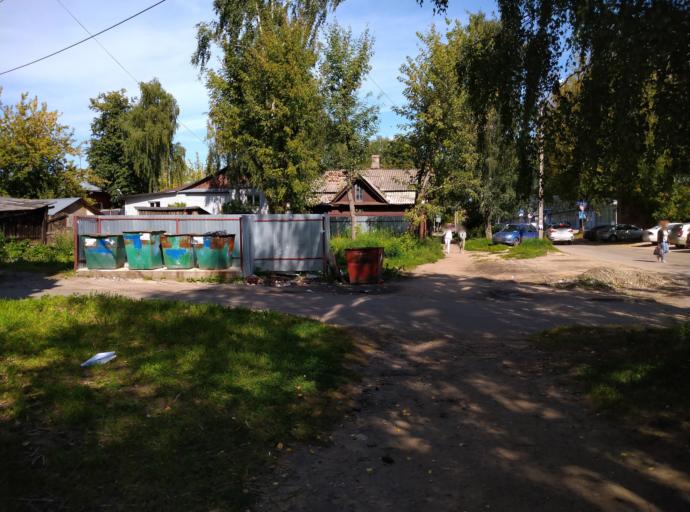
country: RU
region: Kostroma
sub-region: Kostromskoy Rayon
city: Kostroma
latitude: 57.7708
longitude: 40.9374
